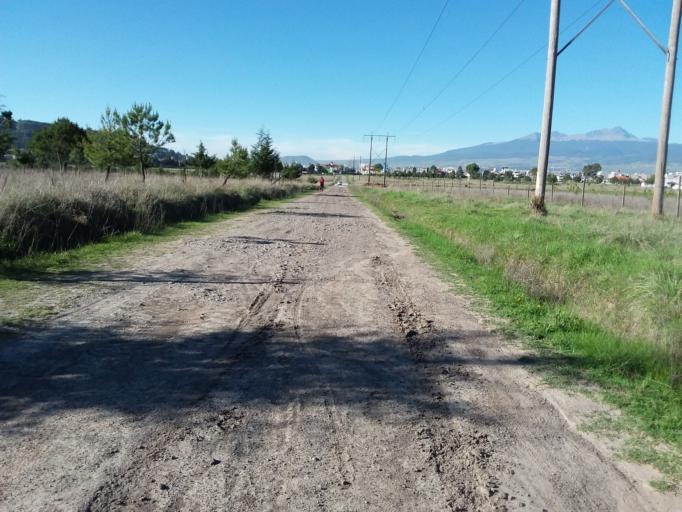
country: MX
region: Mexico
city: San Marcos Yachihuacaltepec
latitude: 19.3106
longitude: -99.6957
